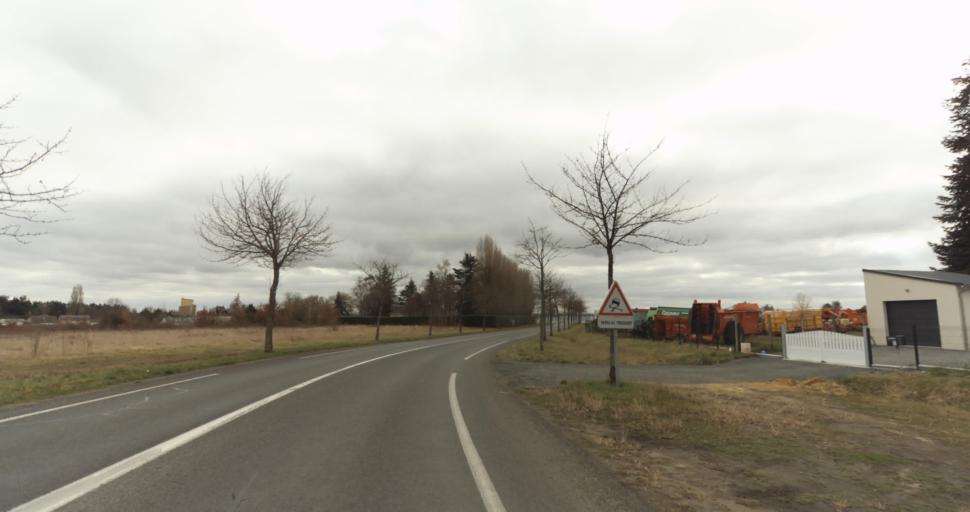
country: FR
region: Pays de la Loire
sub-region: Departement de Maine-et-Loire
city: Saint-Philbert-du-Peuple
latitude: 47.3774
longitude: -0.0987
